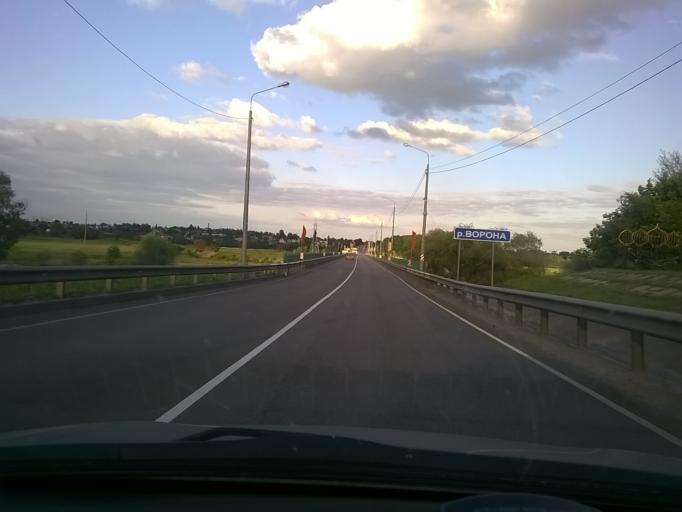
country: RU
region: Voronezj
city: Borisoglebsk
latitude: 51.3762
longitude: 42.0471
